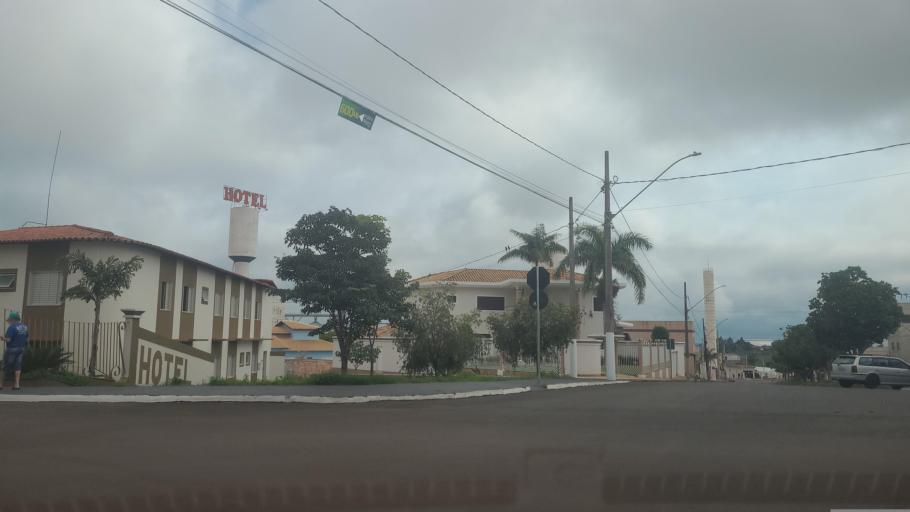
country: BR
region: Minas Gerais
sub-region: Carmo Do Paranaiba
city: Carmo do Paranaiba
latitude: -19.1974
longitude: -46.2373
